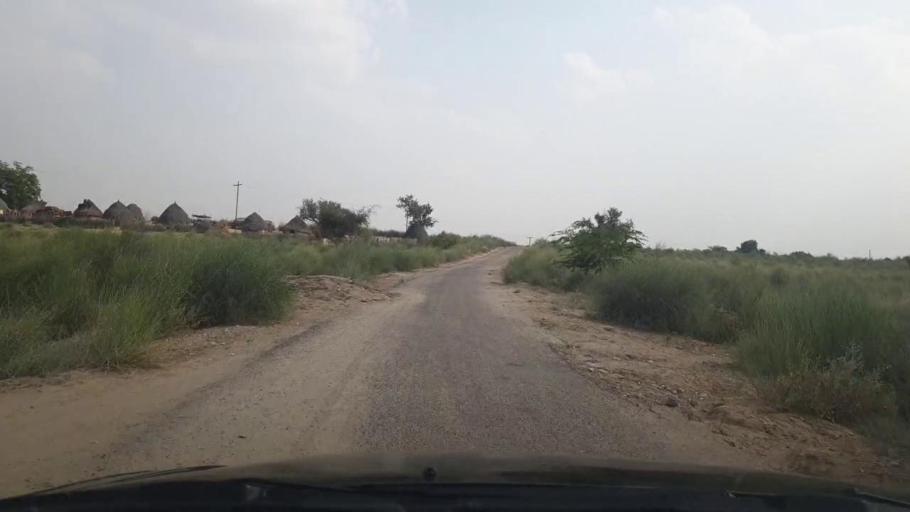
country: PK
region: Sindh
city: Islamkot
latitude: 25.0200
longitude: 70.5938
